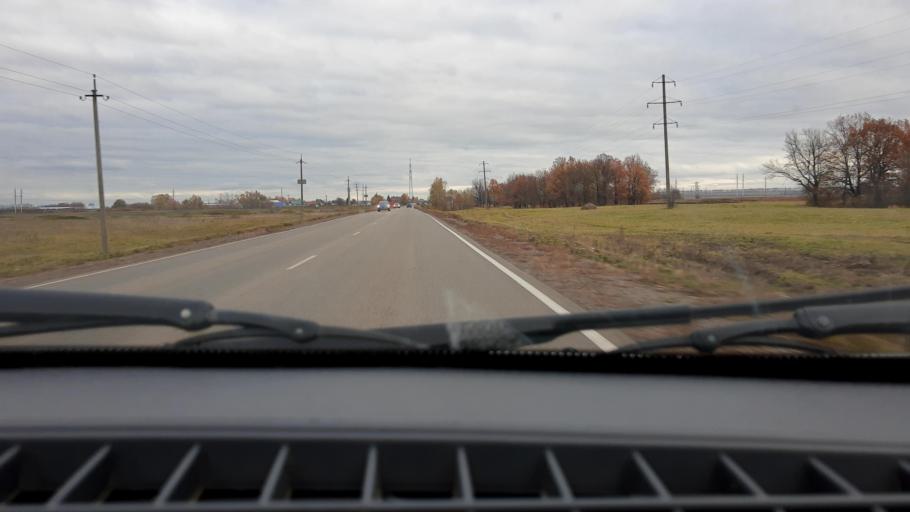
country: RU
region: Bashkortostan
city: Kabakovo
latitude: 54.5570
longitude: 56.0153
